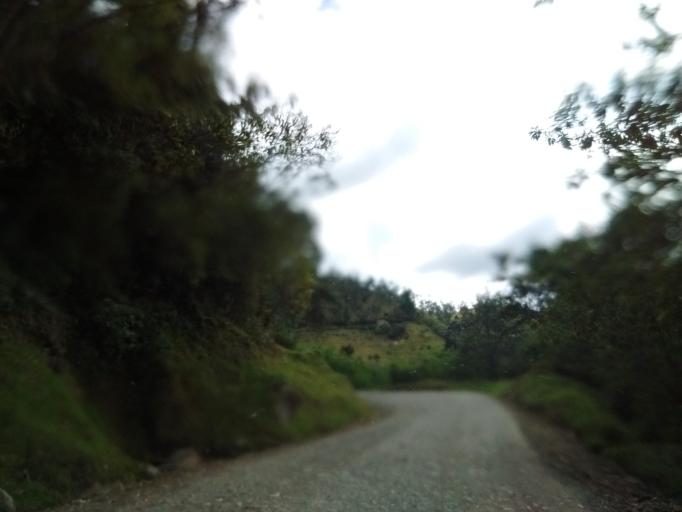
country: CO
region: Cauca
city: Totoro
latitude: 2.3807
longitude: -76.4490
